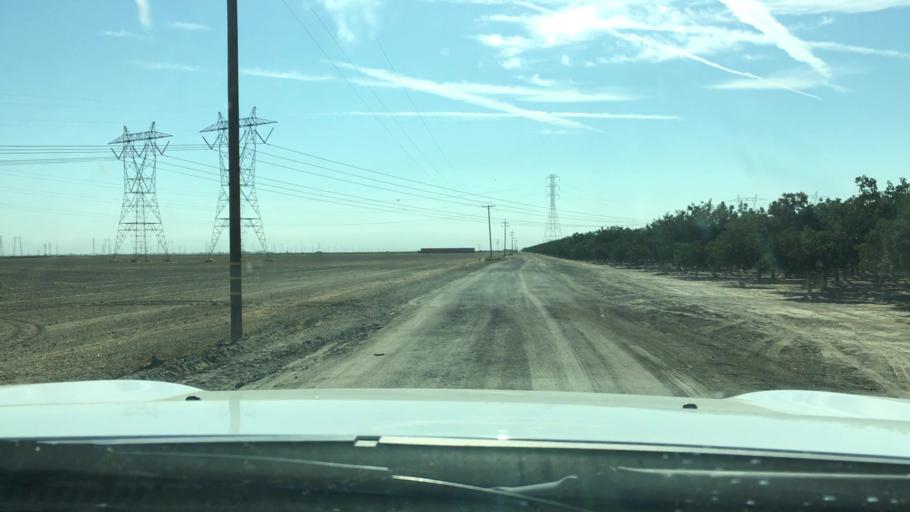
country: US
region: California
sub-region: Kern County
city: Buttonwillow
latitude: 35.3767
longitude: -119.4030
